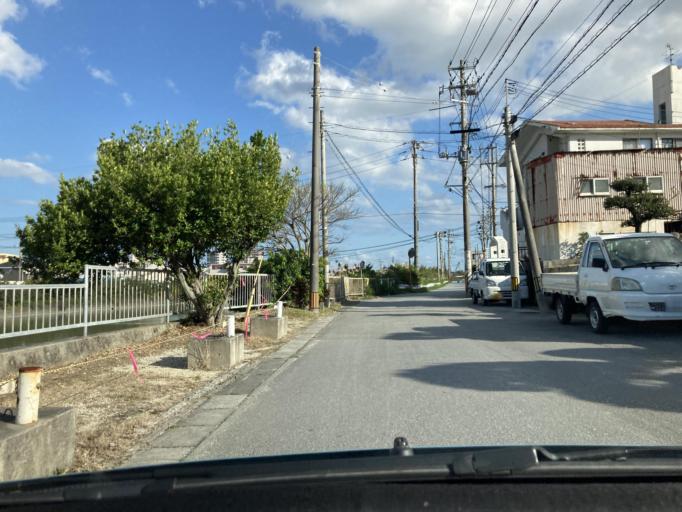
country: JP
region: Okinawa
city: Tomigusuku
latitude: 26.1947
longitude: 127.7001
